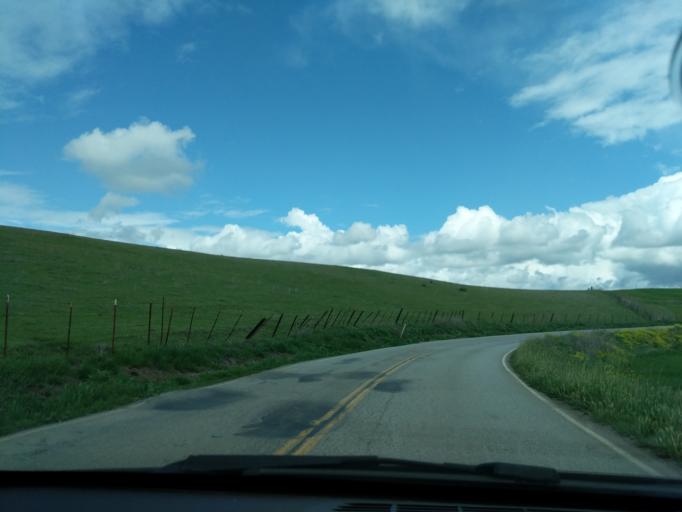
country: US
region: California
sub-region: San Benito County
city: Hollister
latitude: 36.8700
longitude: -121.4354
